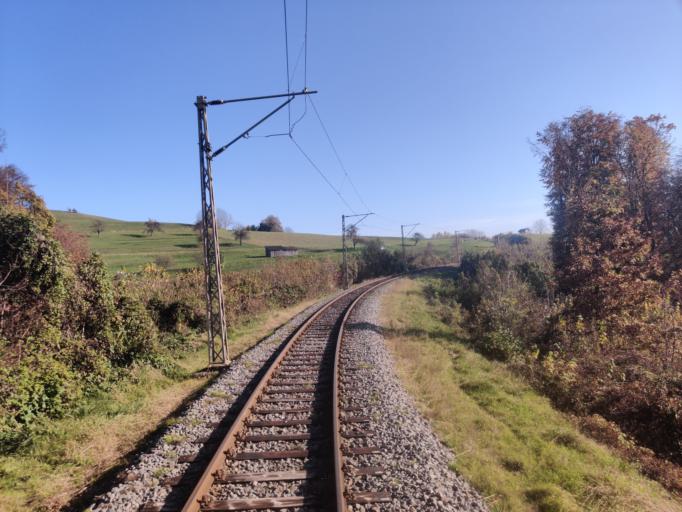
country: AT
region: Styria
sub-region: Politischer Bezirk Suedoststeiermark
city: Maierdorf
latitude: 46.8945
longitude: 15.8688
